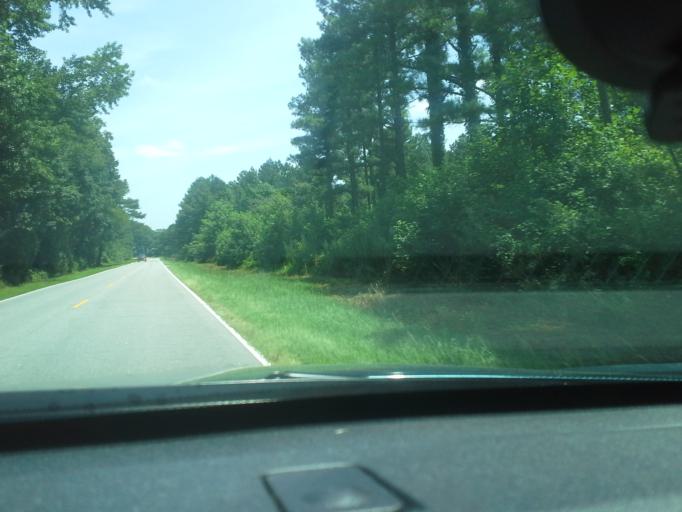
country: US
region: North Carolina
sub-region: Washington County
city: Plymouth
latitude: 35.9101
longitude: -76.6579
